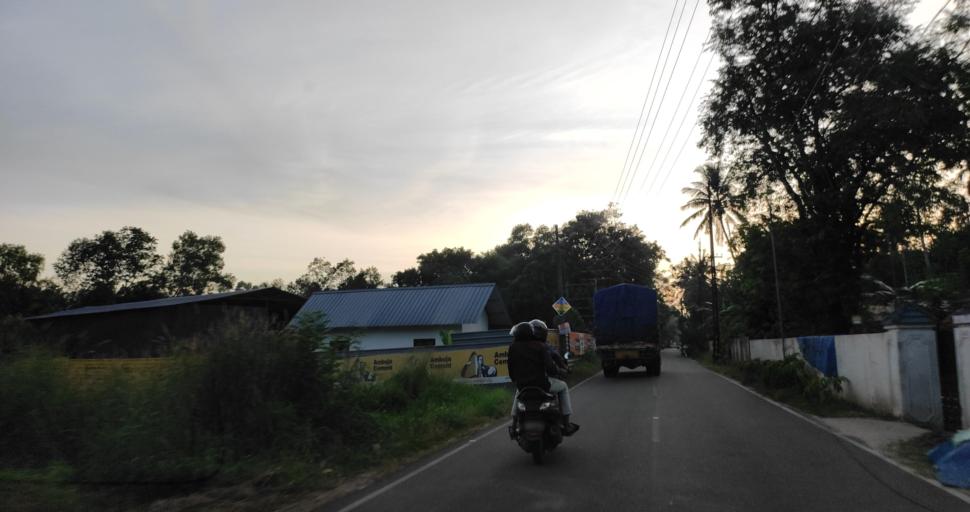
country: IN
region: Kerala
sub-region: Alappuzha
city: Shertallai
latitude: 9.6406
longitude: 76.3503
